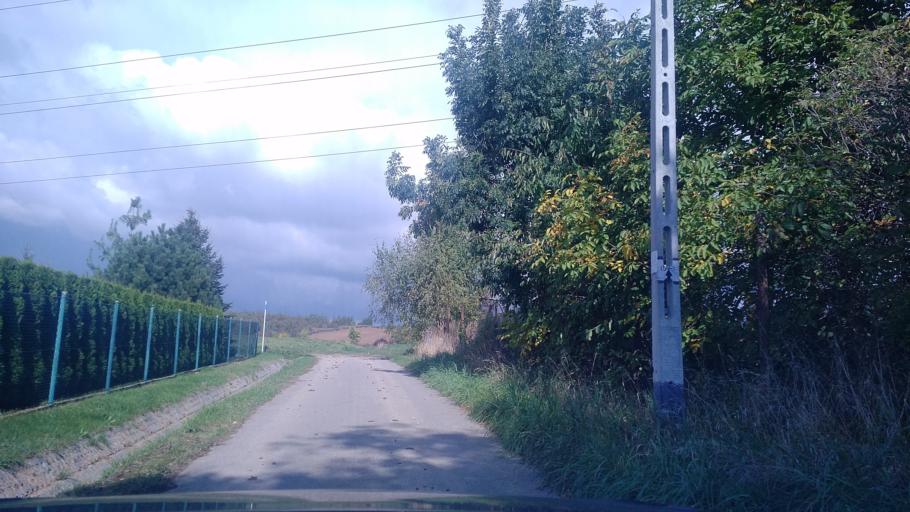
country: PL
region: Lesser Poland Voivodeship
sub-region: Powiat krakowski
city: Wielka Wies
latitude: 50.1378
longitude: 19.8390
